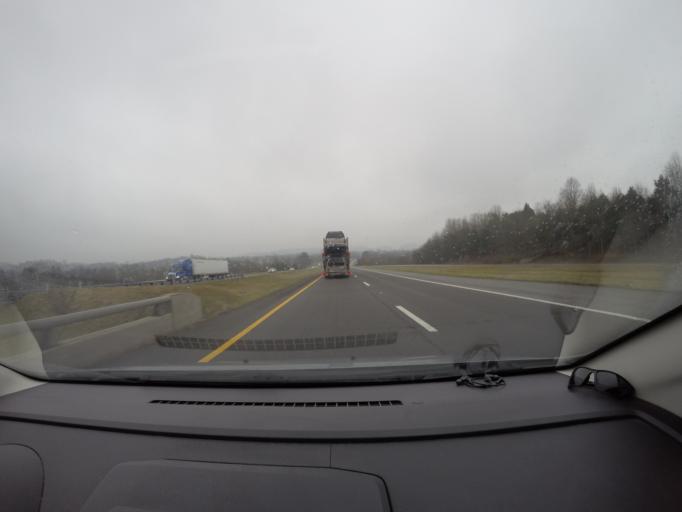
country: US
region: Tennessee
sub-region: Rutherford County
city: Plainview
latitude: 35.6251
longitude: -86.2433
